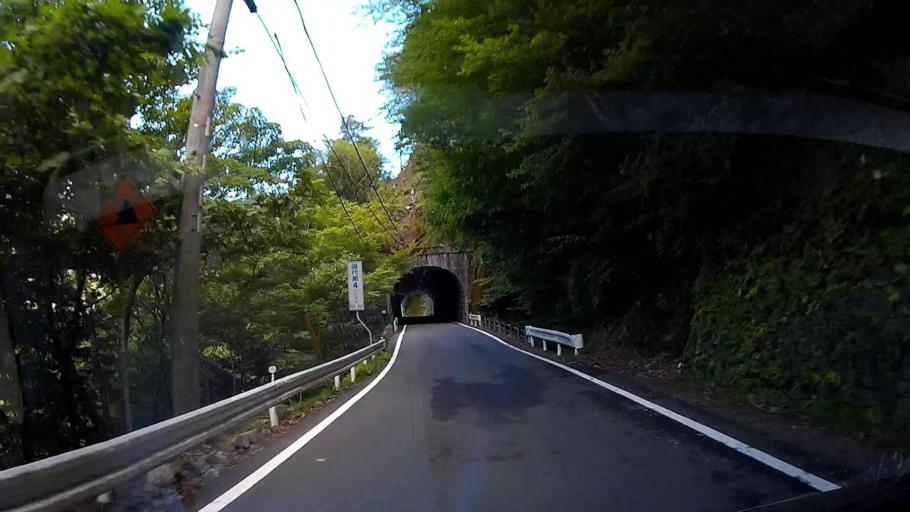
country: JP
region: Shizuoka
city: Shizuoka-shi
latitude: 35.2706
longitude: 138.2232
